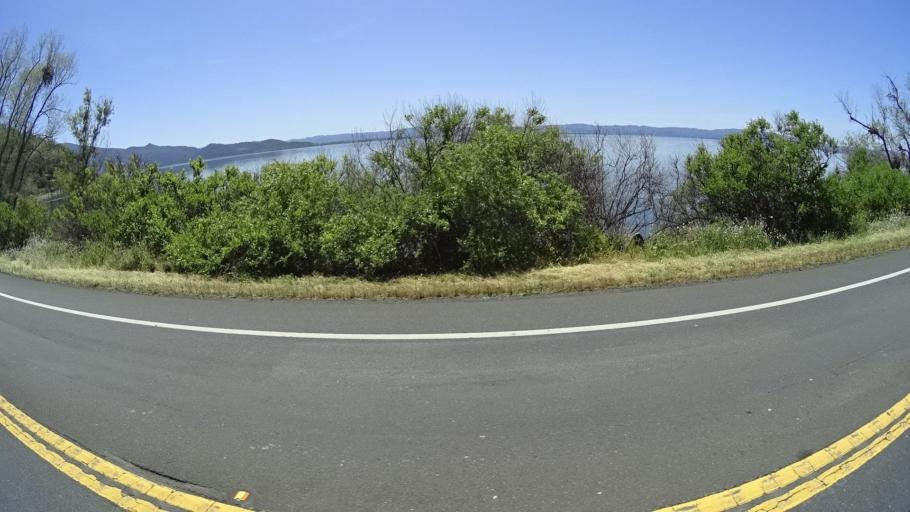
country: US
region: California
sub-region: Lake County
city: Lucerne
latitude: 39.0617
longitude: -122.7825
